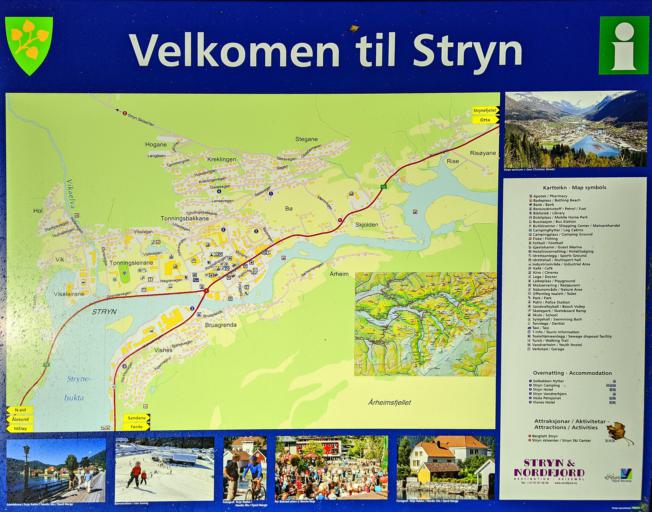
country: NO
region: Sogn og Fjordane
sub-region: Stryn
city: Stryn
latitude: 61.9030
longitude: 6.7225
